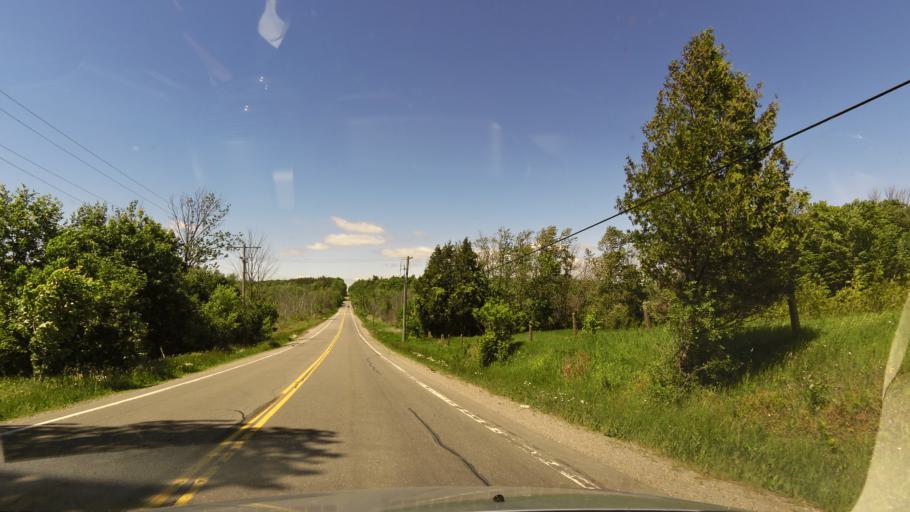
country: CA
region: Ontario
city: Vaughan
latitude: 43.9500
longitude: -79.5340
